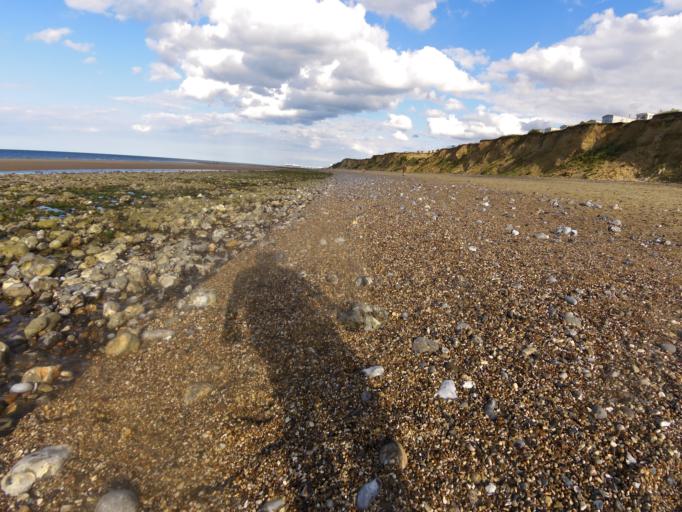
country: GB
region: England
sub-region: Norfolk
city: Cromer
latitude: 52.9375
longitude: 1.2748
